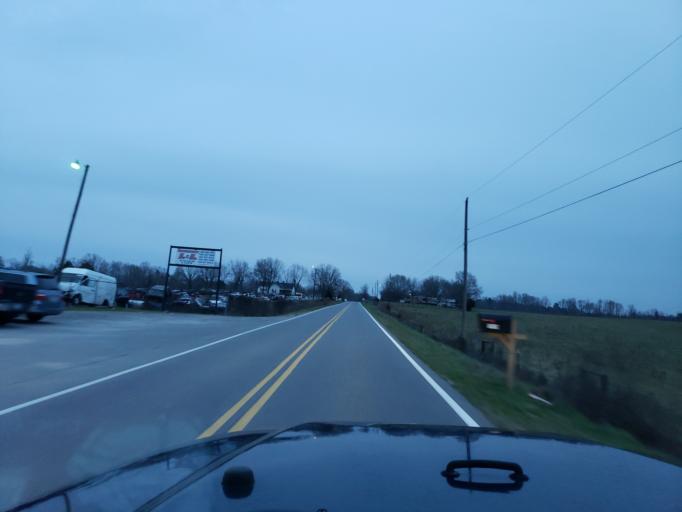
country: US
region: North Carolina
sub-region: Cleveland County
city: White Plains
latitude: 35.2154
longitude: -81.4554
